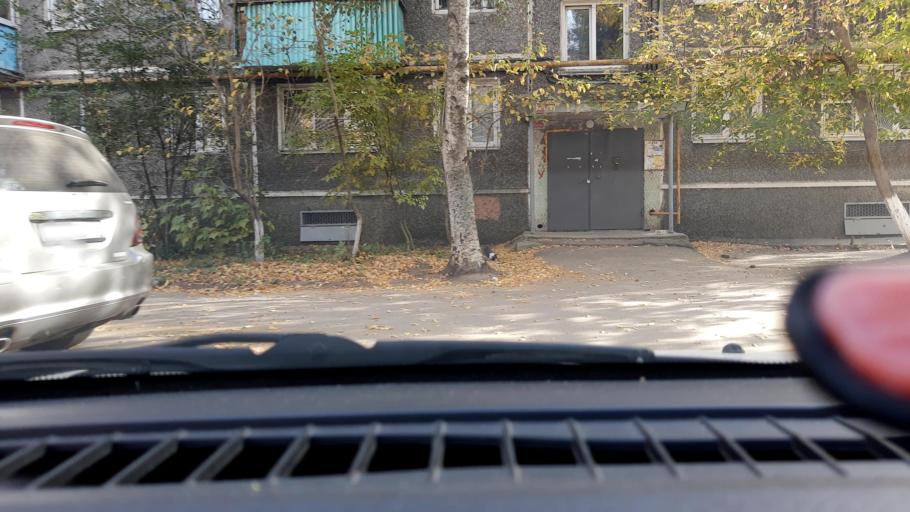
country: RU
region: Nizjnij Novgorod
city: Nizhniy Novgorod
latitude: 56.2793
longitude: 43.9174
